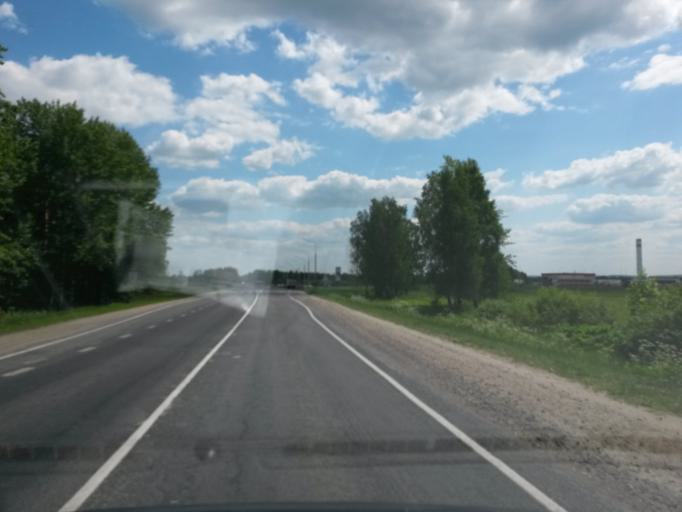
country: RU
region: Jaroslavl
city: Yaroslavl
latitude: 57.5518
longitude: 39.8855
